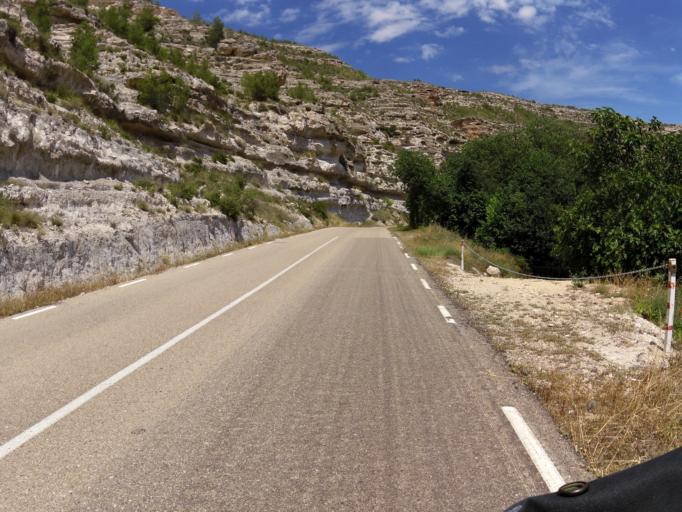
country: ES
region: Castille-La Mancha
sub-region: Provincia de Albacete
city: Jorquera
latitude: 39.1712
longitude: -1.5427
